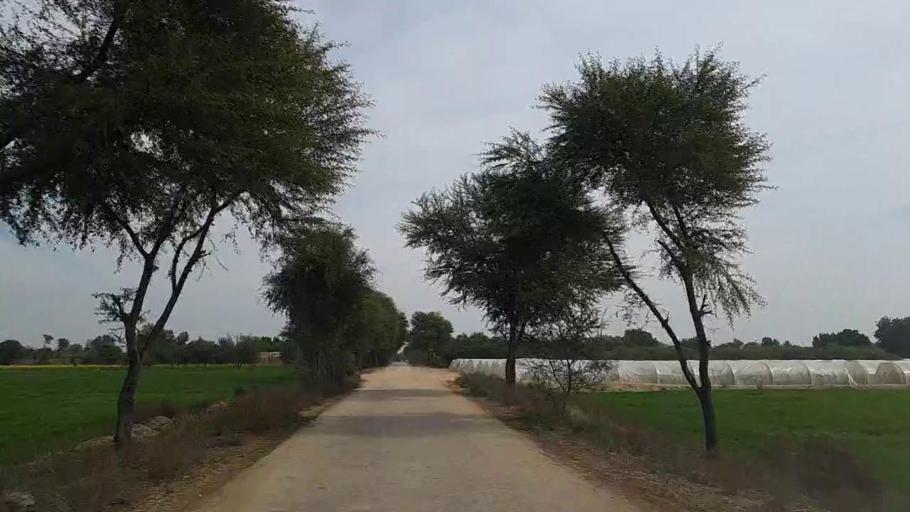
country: PK
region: Sindh
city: Daur
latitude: 26.4105
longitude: 68.4480
